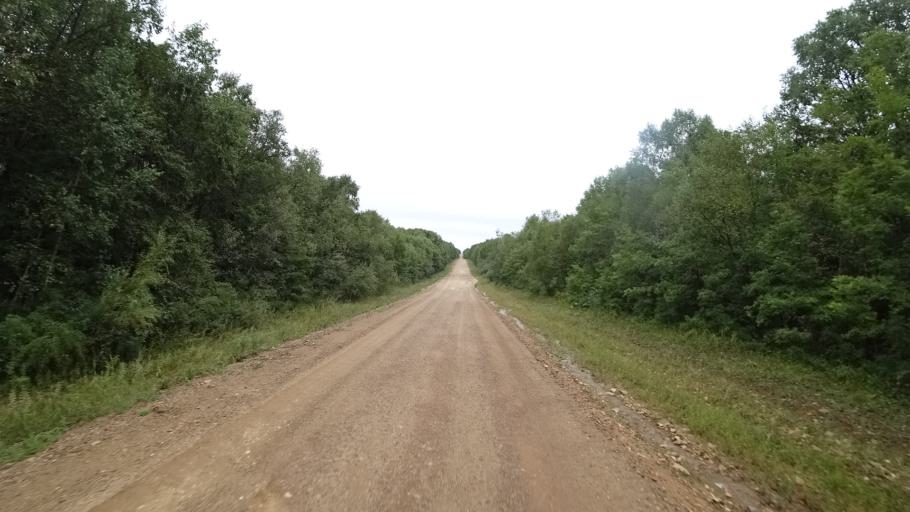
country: RU
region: Primorskiy
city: Ivanovka
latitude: 44.0366
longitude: 132.5353
